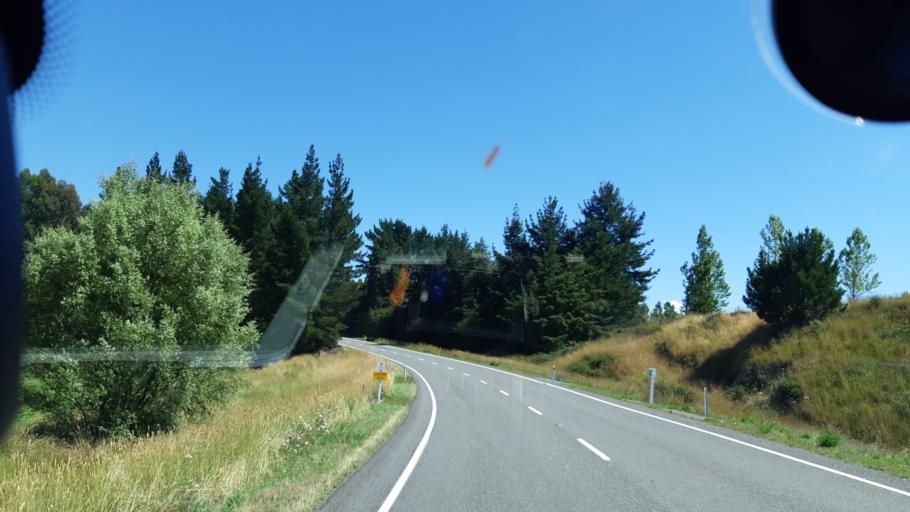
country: NZ
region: Canterbury
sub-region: Kaikoura District
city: Kaikoura
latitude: -42.7523
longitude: 173.2725
